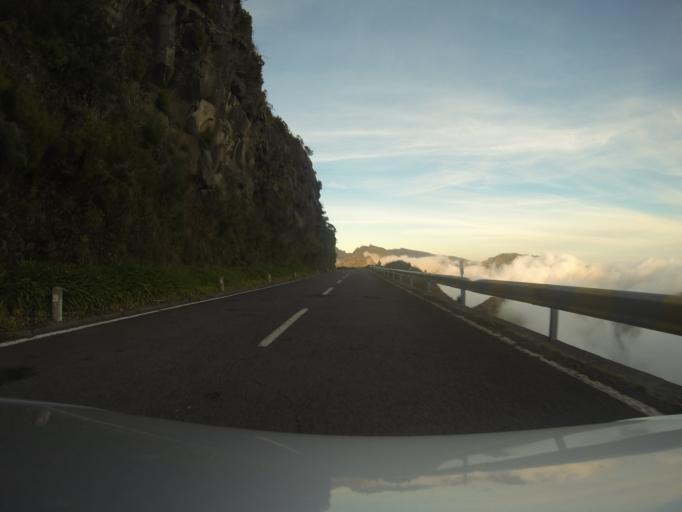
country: PT
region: Madeira
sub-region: Sao Vicente
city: Sao Vicente
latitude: 32.7376
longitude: -17.0496
